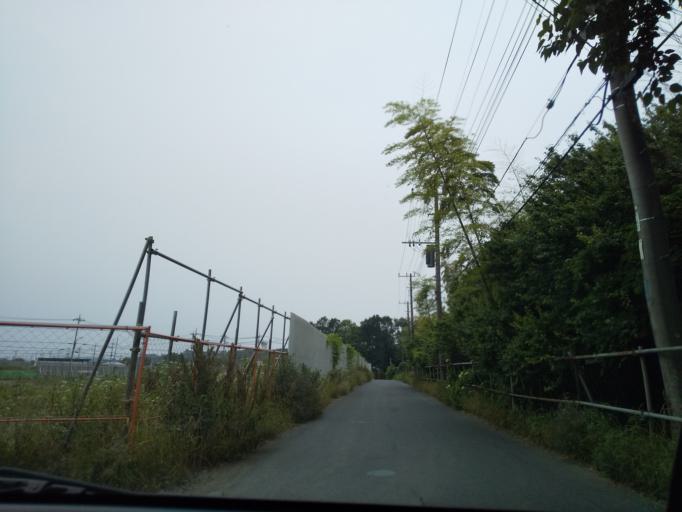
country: JP
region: Kanagawa
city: Zama
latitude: 35.5206
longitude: 139.3951
